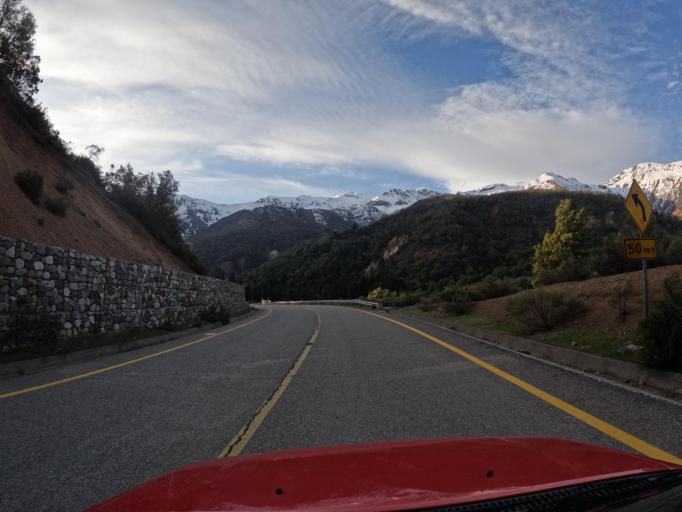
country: CL
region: Maule
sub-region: Provincia de Linares
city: Colbun
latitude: -35.8257
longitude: -70.7665
